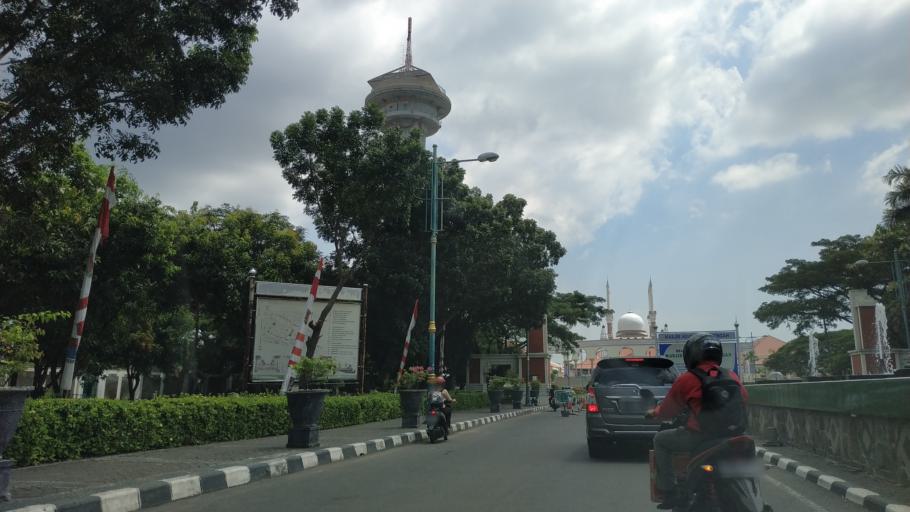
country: ID
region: Central Java
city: Semarang
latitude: -6.9849
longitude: 110.4482
